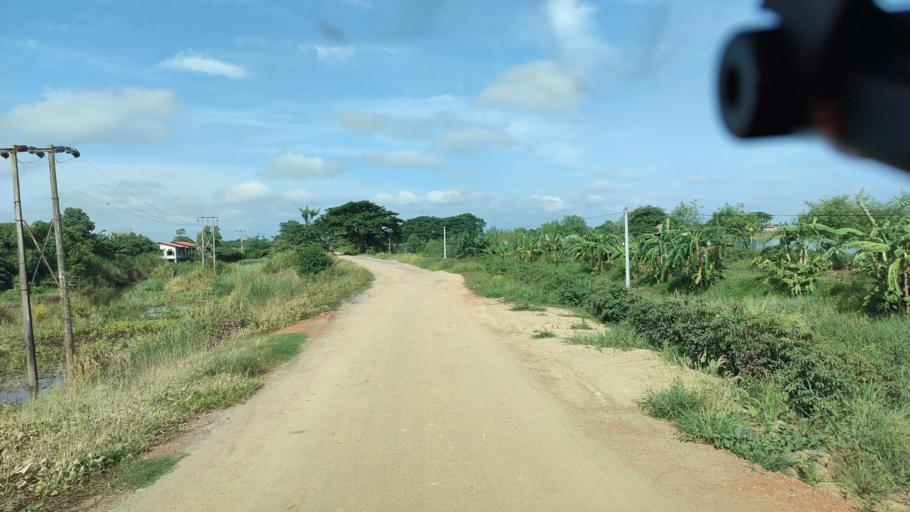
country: MM
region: Bago
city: Letpandan
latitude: 17.7664
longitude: 95.6900
